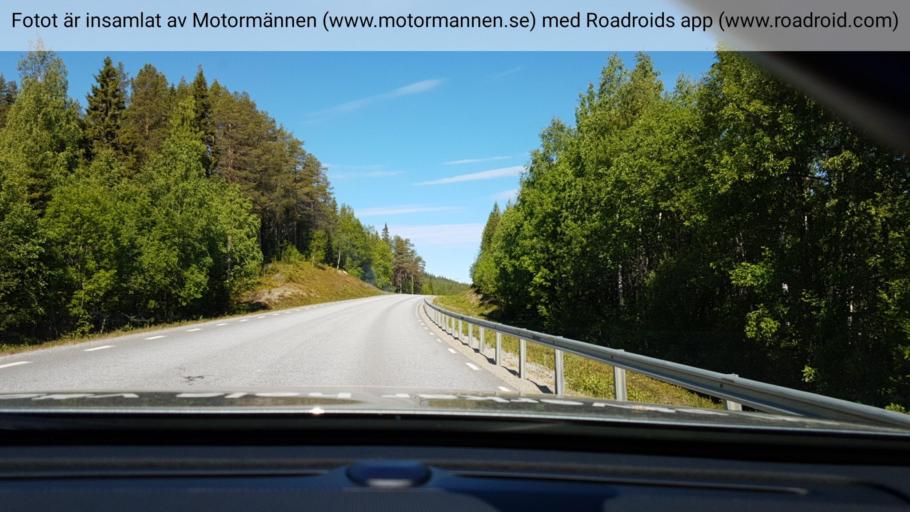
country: SE
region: Vaesterbotten
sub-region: Lycksele Kommun
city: Lycksele
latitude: 64.0395
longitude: 18.5910
